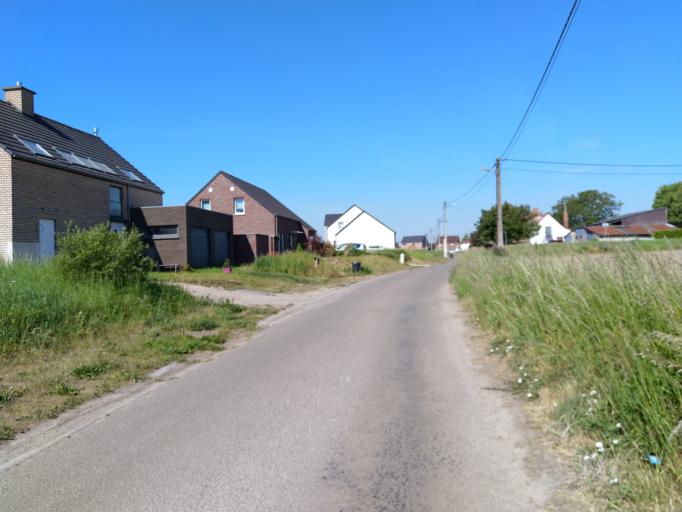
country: BE
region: Wallonia
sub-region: Province du Hainaut
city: Lens
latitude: 50.5492
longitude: 3.8899
